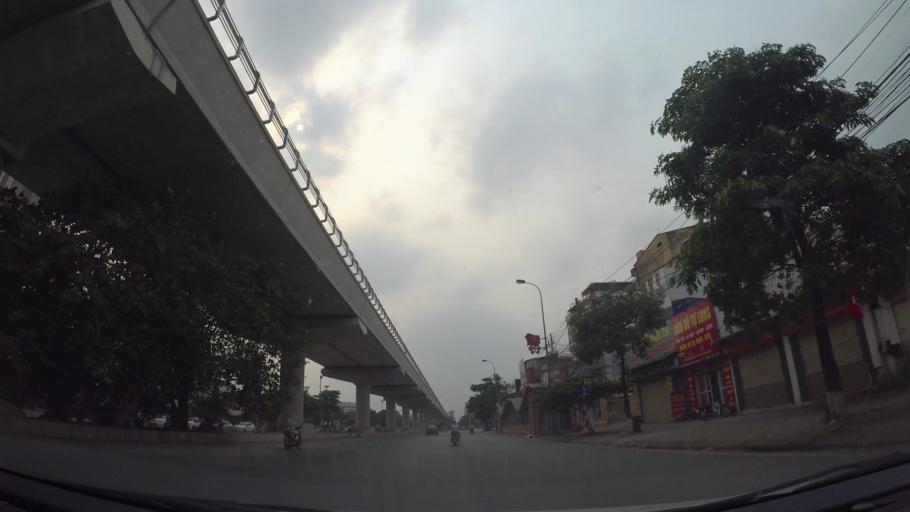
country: VN
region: Ha Noi
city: Cau Dien
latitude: 21.0461
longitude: 105.7497
